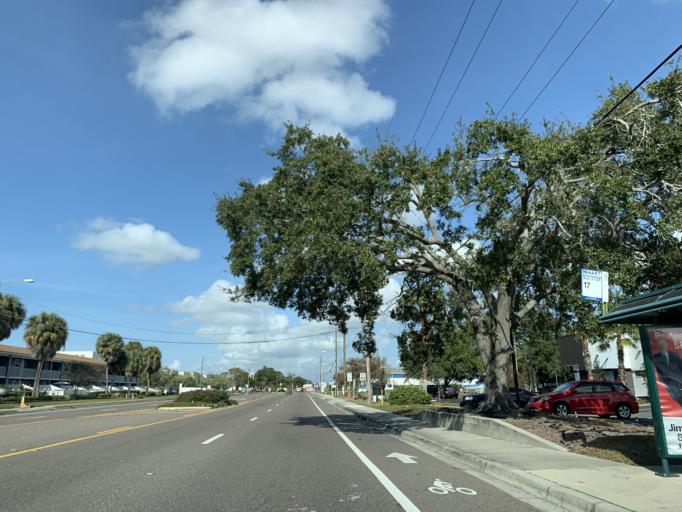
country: US
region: Florida
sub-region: Hillsborough County
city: Tampa
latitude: 27.9031
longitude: -82.5184
